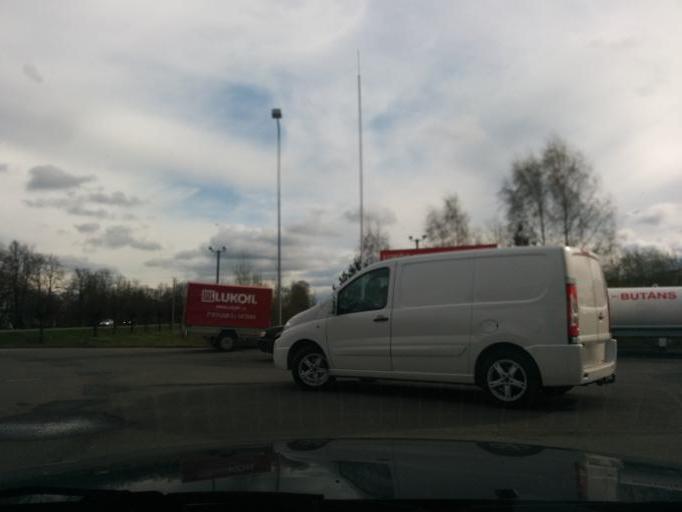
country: LV
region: Jelgava
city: Jelgava
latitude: 56.6242
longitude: 23.7239
